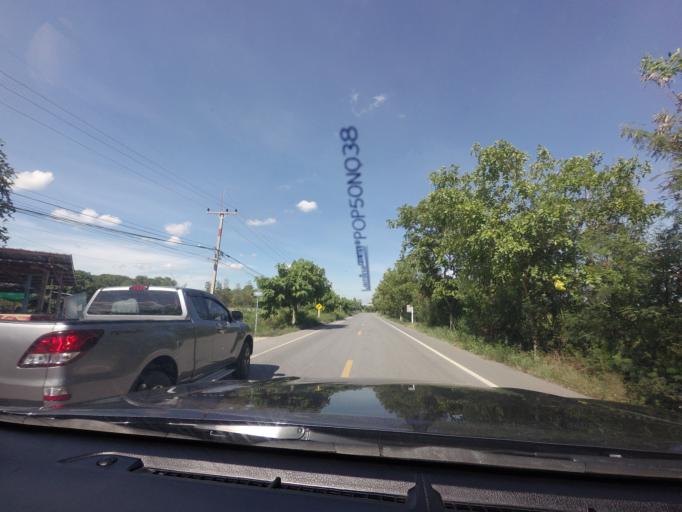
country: TH
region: Suphan Buri
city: Song Phi Nong
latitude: 14.1732
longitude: 100.0187
